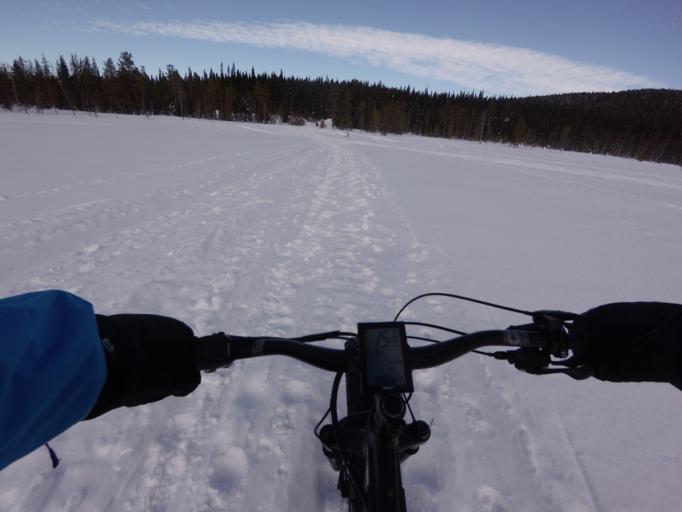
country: FI
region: Lapland
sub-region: Tunturi-Lappi
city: Kolari
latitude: 67.6018
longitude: 24.2192
